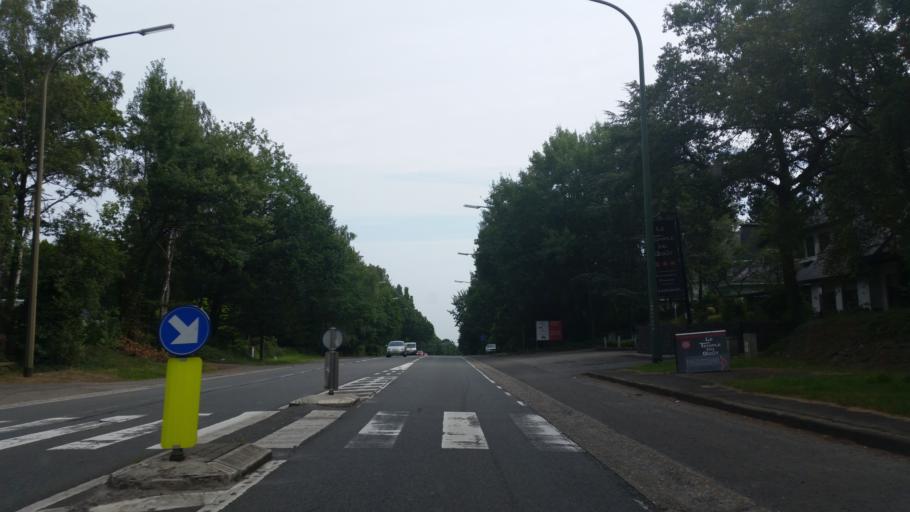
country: BE
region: Wallonia
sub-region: Province de Liege
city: Liege
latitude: 50.5949
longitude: 5.5743
